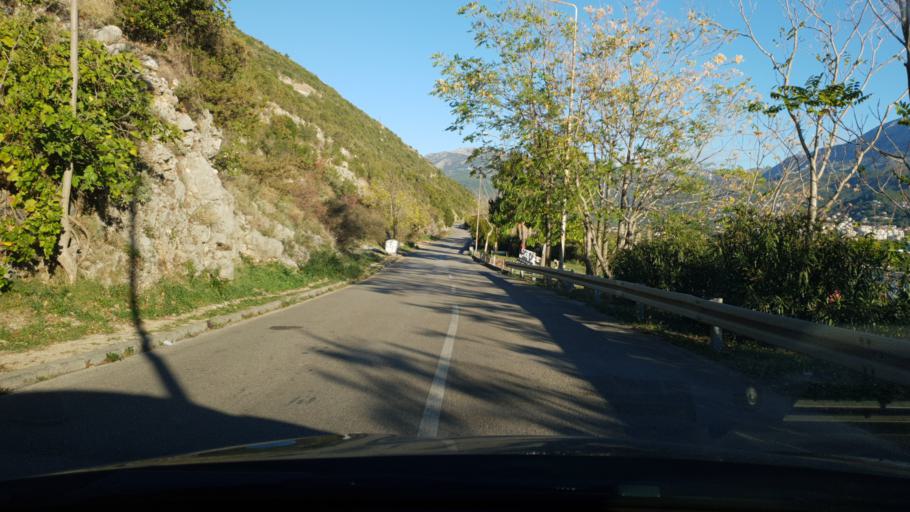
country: ME
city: Igalo
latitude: 42.4408
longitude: 18.5083
